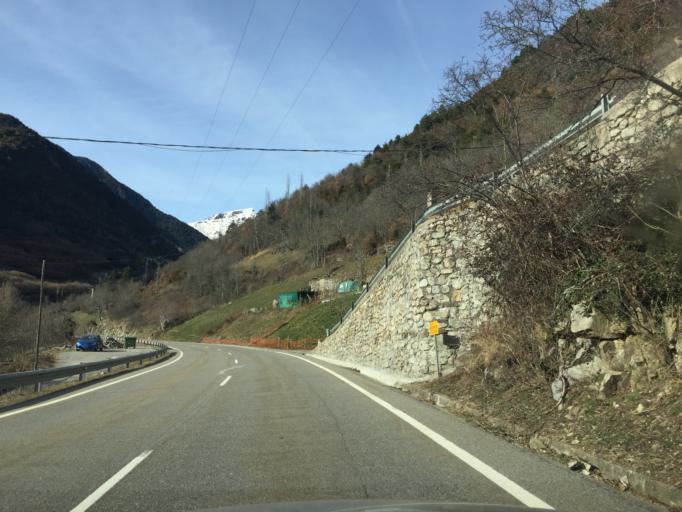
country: ES
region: Aragon
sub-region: Provincia de Huesca
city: Bielsa
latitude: 42.6348
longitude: 0.2204
